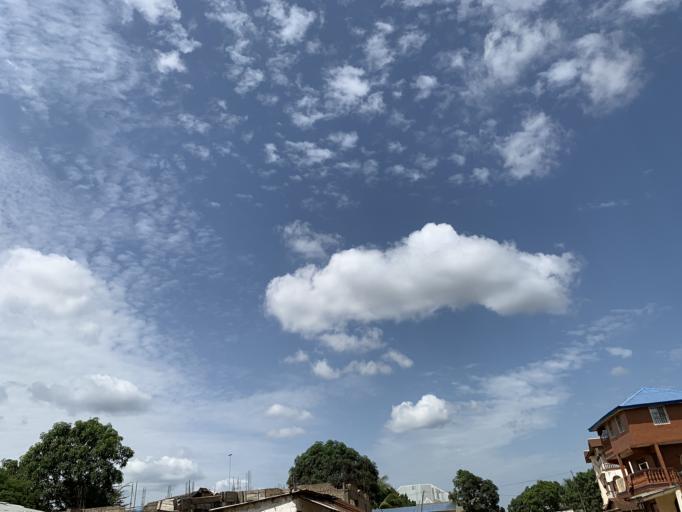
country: SL
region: Western Area
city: Waterloo
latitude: 8.3269
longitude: -13.0508
